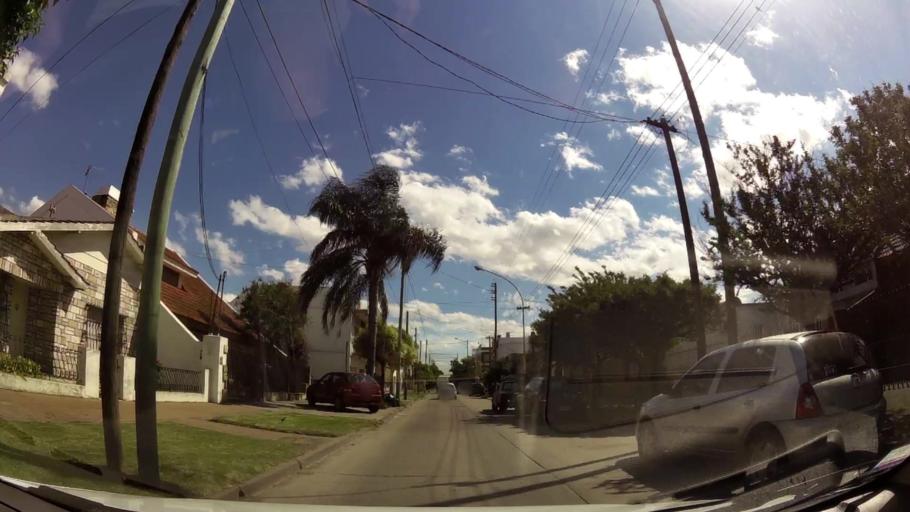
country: AR
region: Buenos Aires
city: San Justo
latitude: -34.6558
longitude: -58.5295
